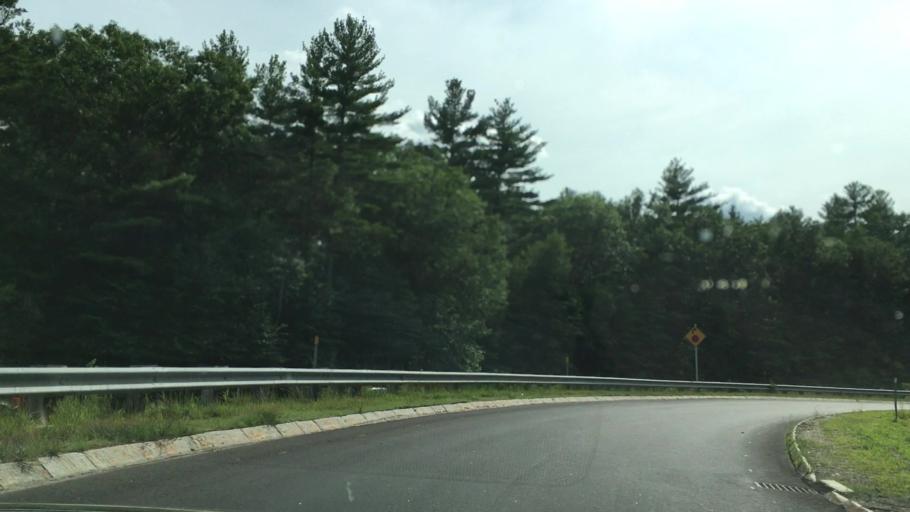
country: US
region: New Hampshire
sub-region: Merrimack County
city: Concord
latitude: 43.1784
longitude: -71.5663
